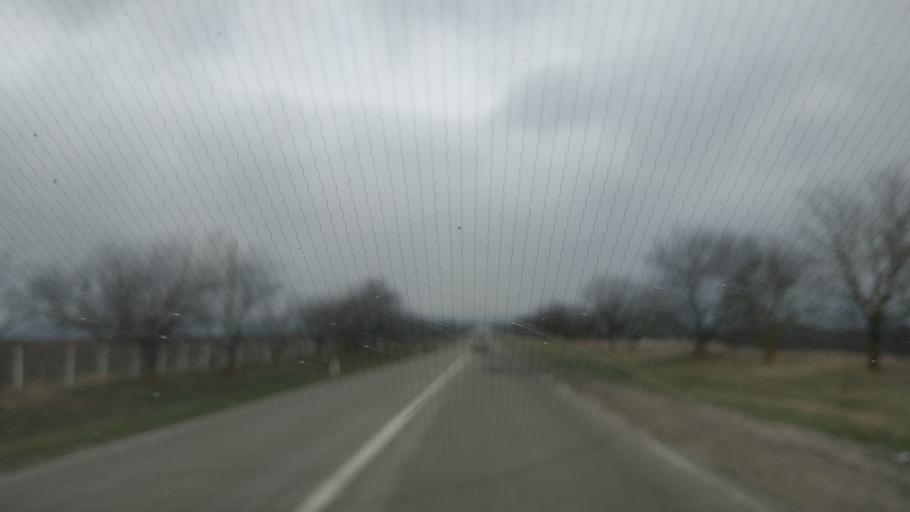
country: MD
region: Gagauzia
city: Comrat
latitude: 46.2662
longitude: 28.7369
